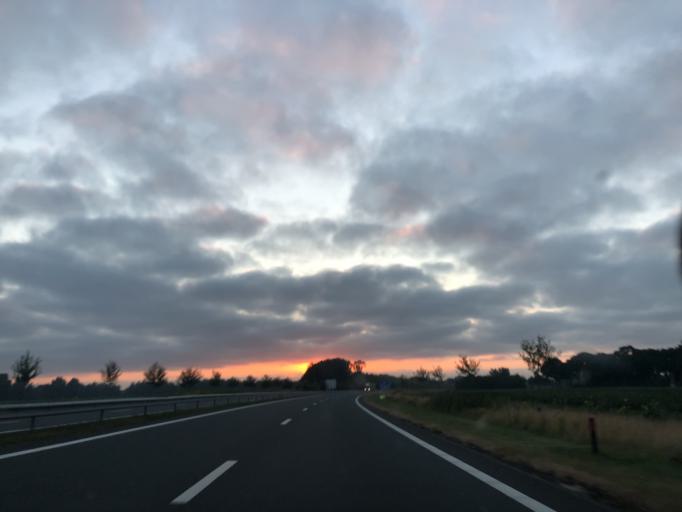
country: NL
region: Groningen
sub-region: Gemeente Veendam
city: Veendam
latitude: 53.0461
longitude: 6.8338
